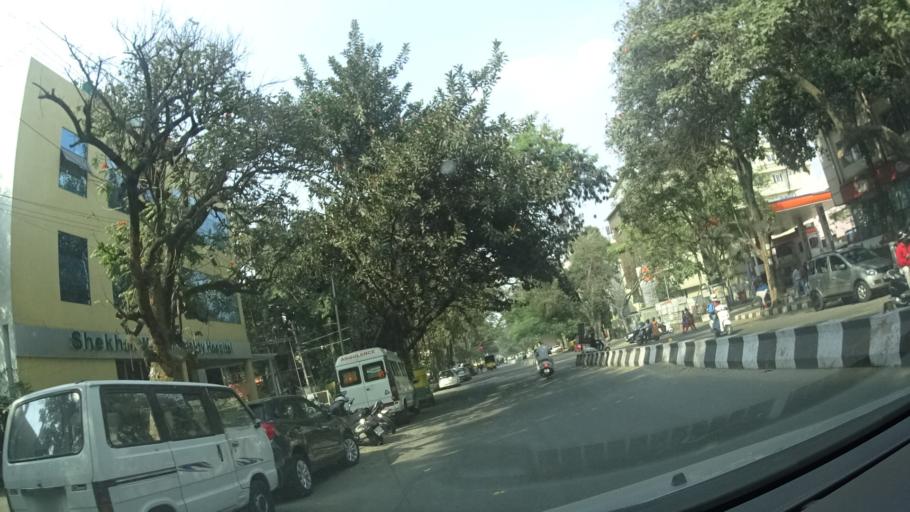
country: IN
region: Karnataka
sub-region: Bangalore Urban
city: Bangalore
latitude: 12.9456
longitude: 77.5678
